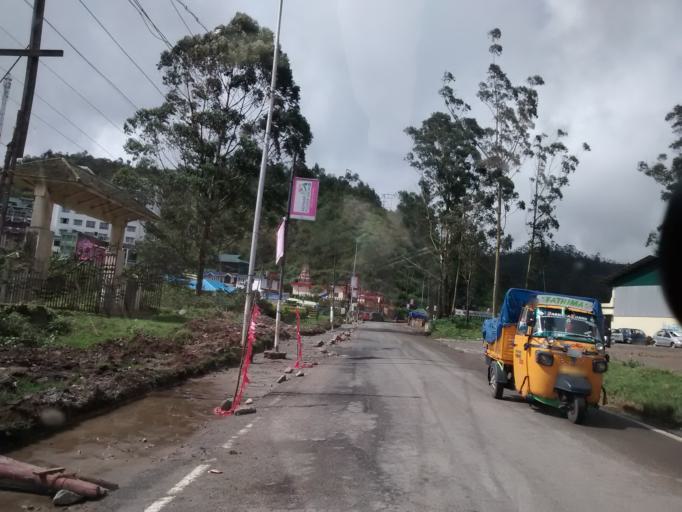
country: IN
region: Kerala
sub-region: Idukki
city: Munnar
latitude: 10.0729
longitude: 77.0617
